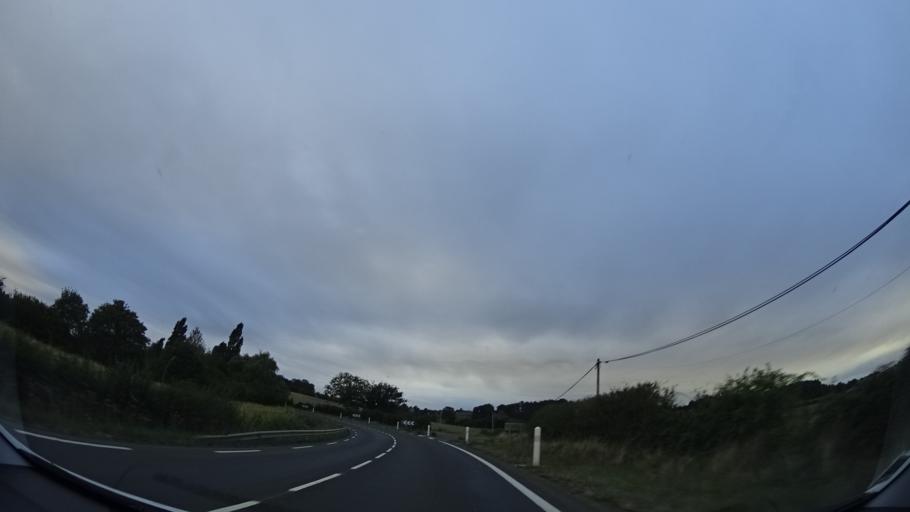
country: FR
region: Pays de la Loire
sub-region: Departement de la Sarthe
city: Coulans-sur-Gee
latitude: 48.0192
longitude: -0.0029
